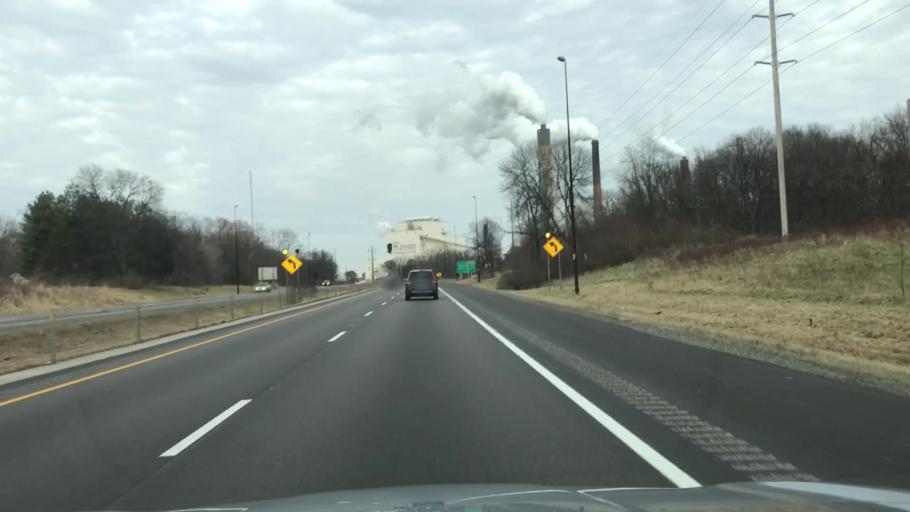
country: US
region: Illinois
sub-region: Sangamon County
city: Southern View
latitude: 39.7512
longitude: -89.6135
